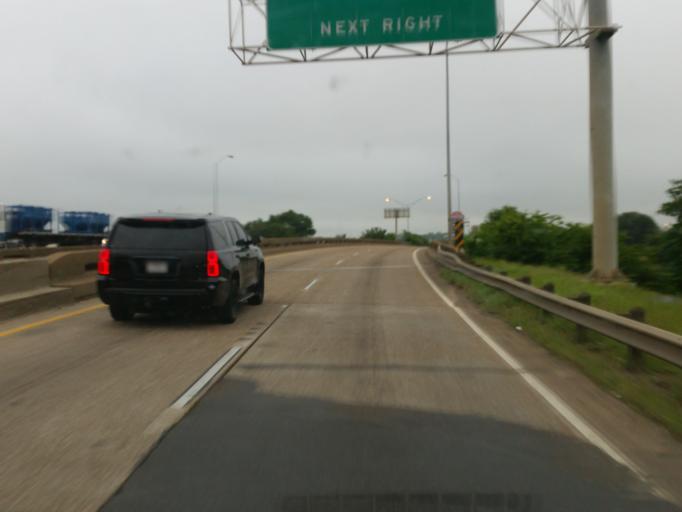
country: US
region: Louisiana
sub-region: Bossier Parish
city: Bossier City
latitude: 32.5236
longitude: -93.7052
